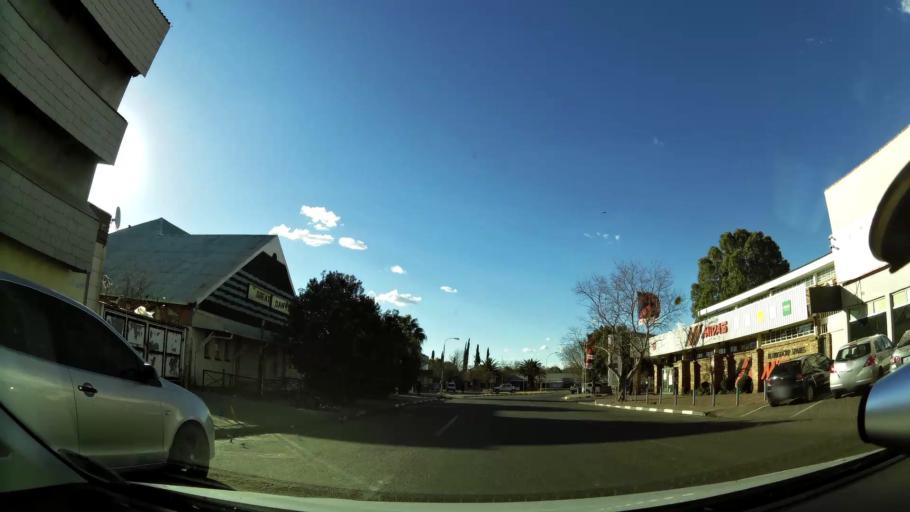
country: ZA
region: North-West
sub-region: Dr Kenneth Kaunda District Municipality
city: Klerksdorp
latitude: -26.8643
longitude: 26.6680
